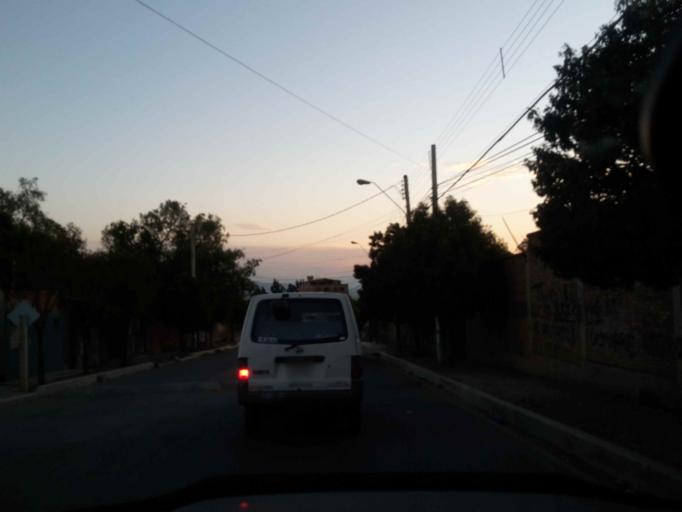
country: BO
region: Cochabamba
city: Cochabamba
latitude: -17.3430
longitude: -66.2037
